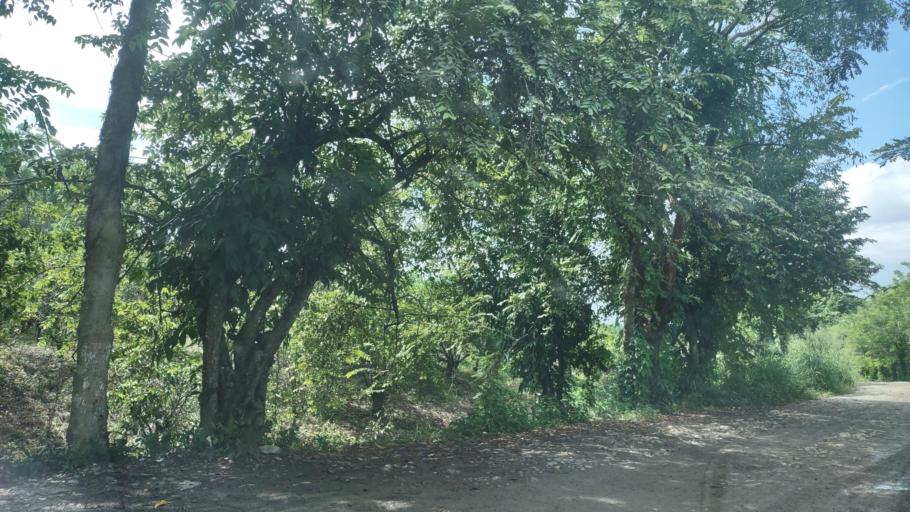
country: MX
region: Veracruz
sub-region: Atzalan
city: Colonias Pedernales
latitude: 20.0568
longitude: -97.0115
